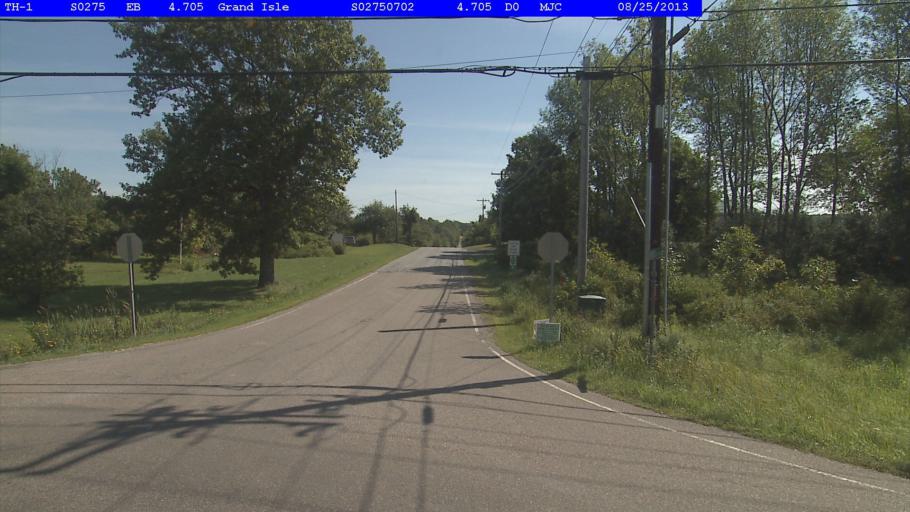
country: US
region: Vermont
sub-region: Grand Isle County
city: North Hero
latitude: 44.7416
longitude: -73.2894
